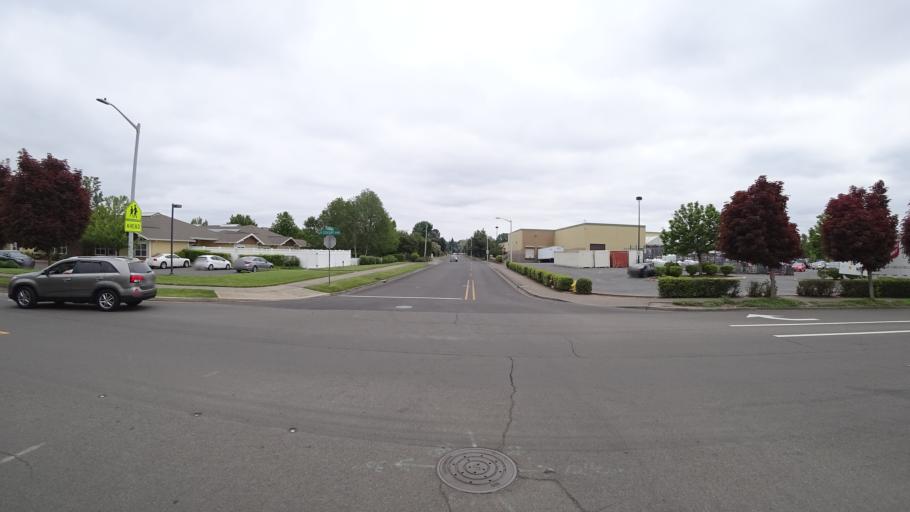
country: US
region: Oregon
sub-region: Washington County
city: Aloha
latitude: 45.5006
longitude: -122.9171
